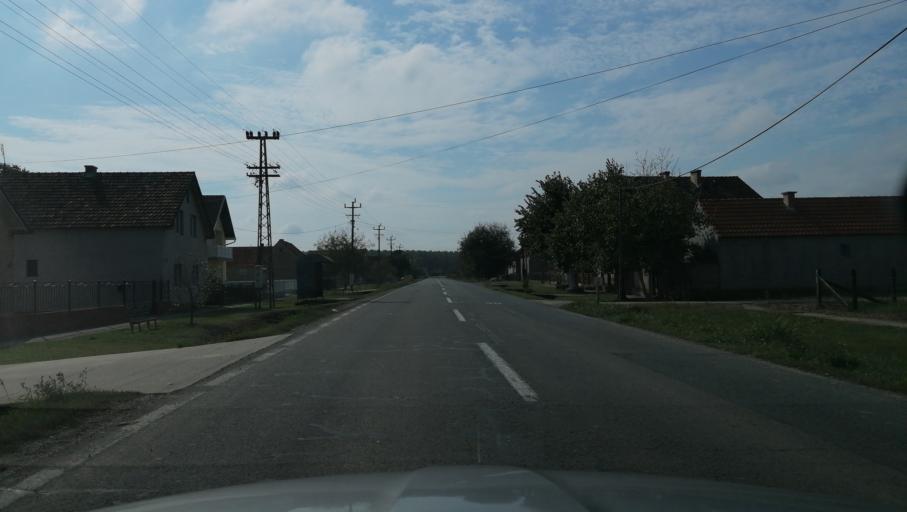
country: RS
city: Bosut
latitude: 44.9278
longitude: 19.3582
